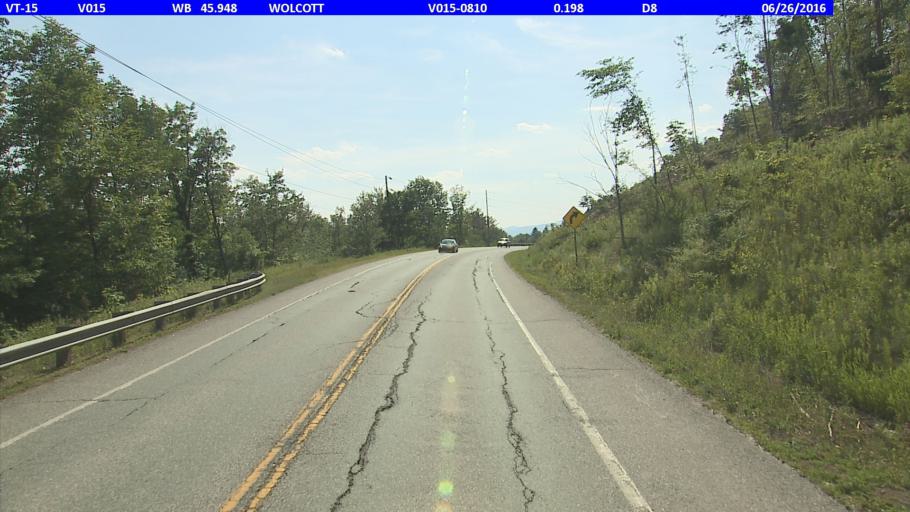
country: US
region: Vermont
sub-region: Lamoille County
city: Morrisville
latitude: 44.5698
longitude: -72.5238
